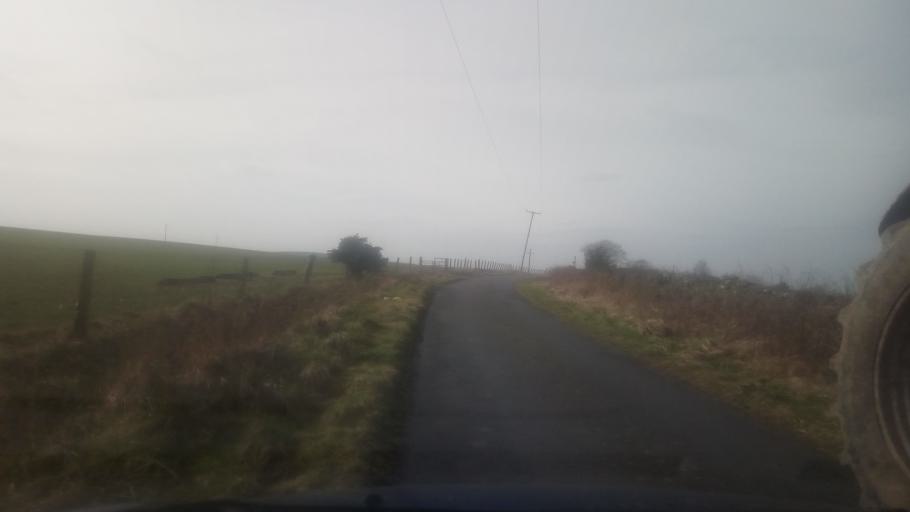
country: GB
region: Scotland
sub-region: The Scottish Borders
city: Hawick
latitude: 55.4045
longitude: -2.6695
